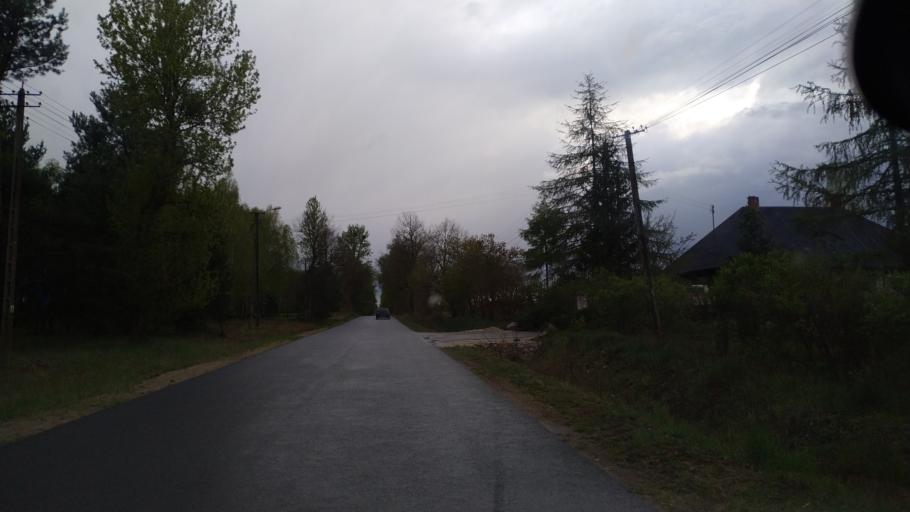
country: PL
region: Pomeranian Voivodeship
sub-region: Powiat starogardzki
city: Osiek
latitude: 53.6435
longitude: 18.4866
